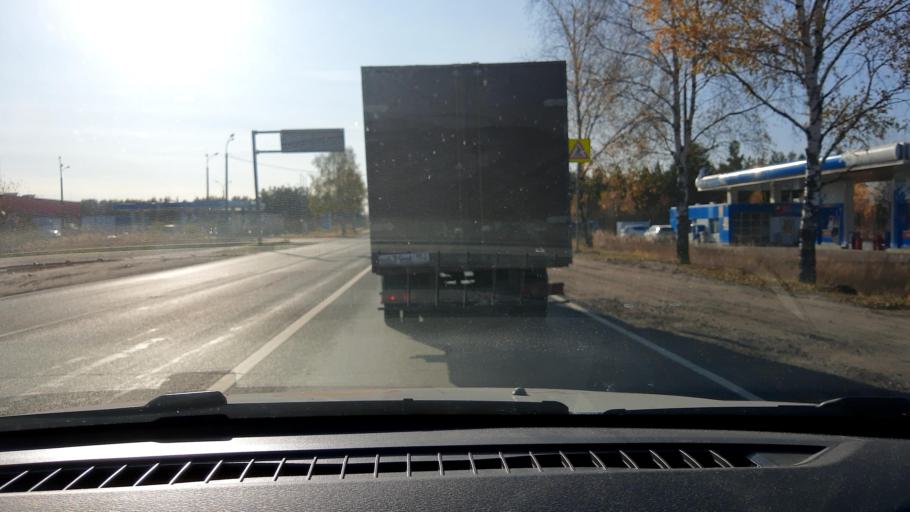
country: RU
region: Nizjnij Novgorod
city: Dzerzhinsk
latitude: 56.2946
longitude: 43.4761
